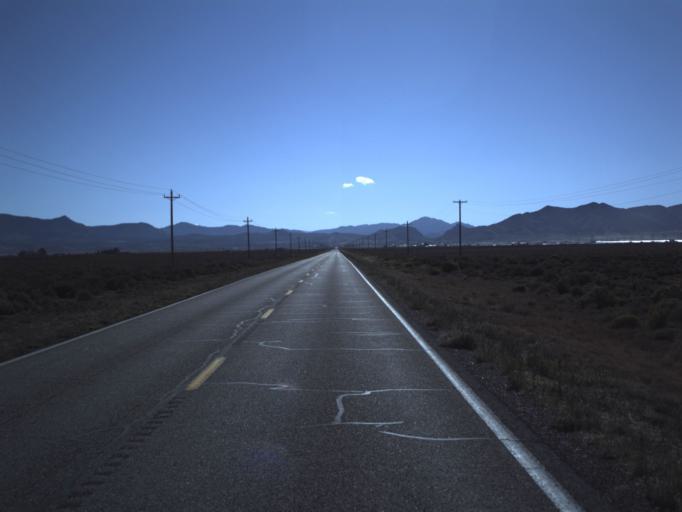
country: US
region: Utah
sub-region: Washington County
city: Enterprise
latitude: 37.6973
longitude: -113.6225
